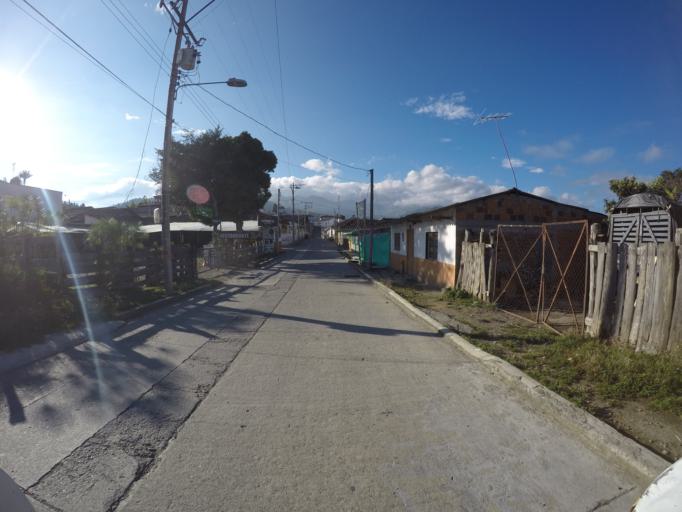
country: CO
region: Quindio
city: Salento
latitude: 4.6396
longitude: -75.5716
